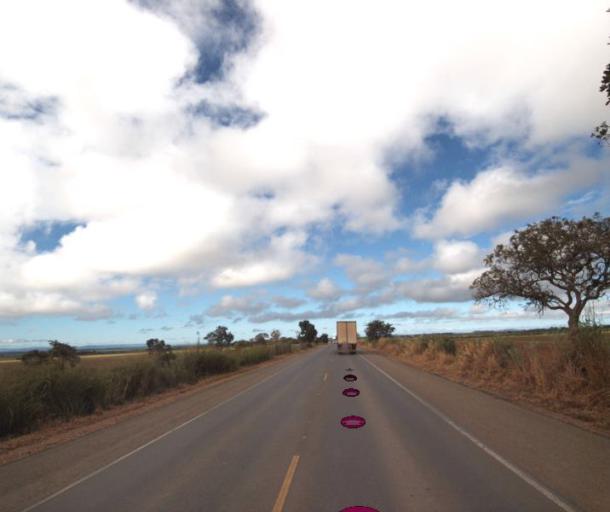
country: BR
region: Goias
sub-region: Uruacu
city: Uruacu
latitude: -14.7678
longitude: -49.2642
